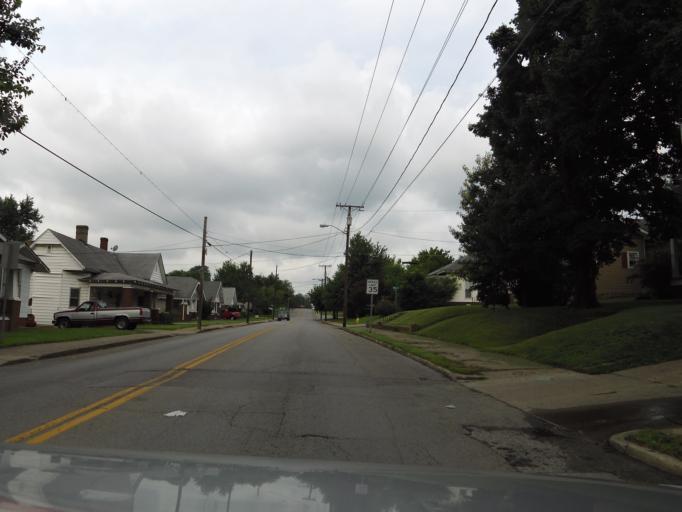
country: US
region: Kentucky
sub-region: Hopkins County
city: Madisonville
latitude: 37.3331
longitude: -87.4989
